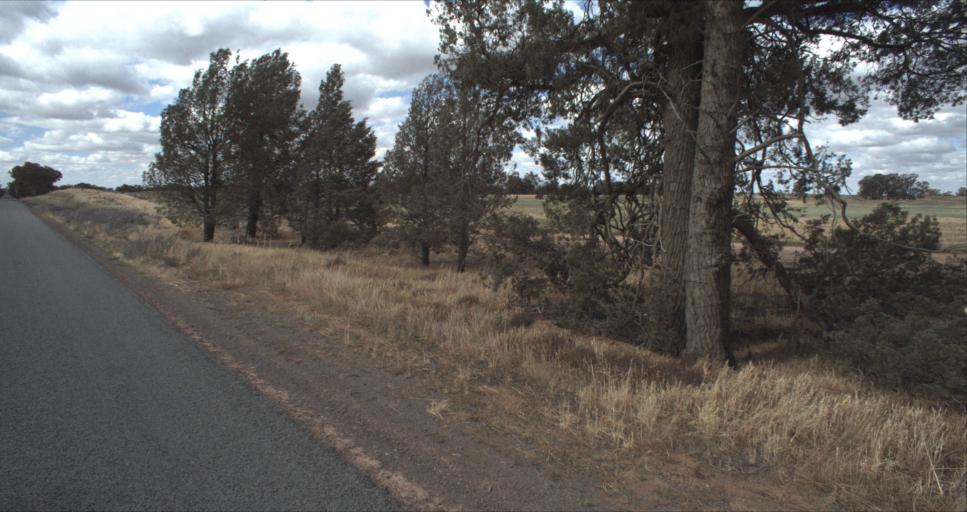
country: AU
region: New South Wales
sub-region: Leeton
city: Leeton
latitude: -34.6752
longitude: 146.3467
